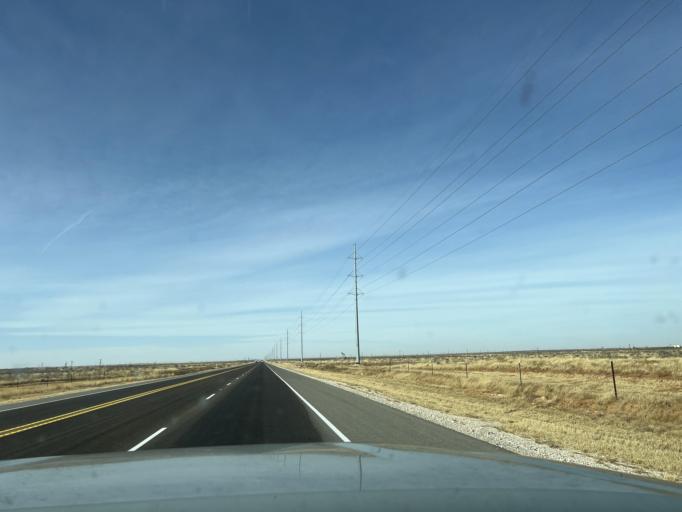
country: US
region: Texas
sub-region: Andrews County
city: Andrews
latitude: 32.3422
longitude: -102.6964
